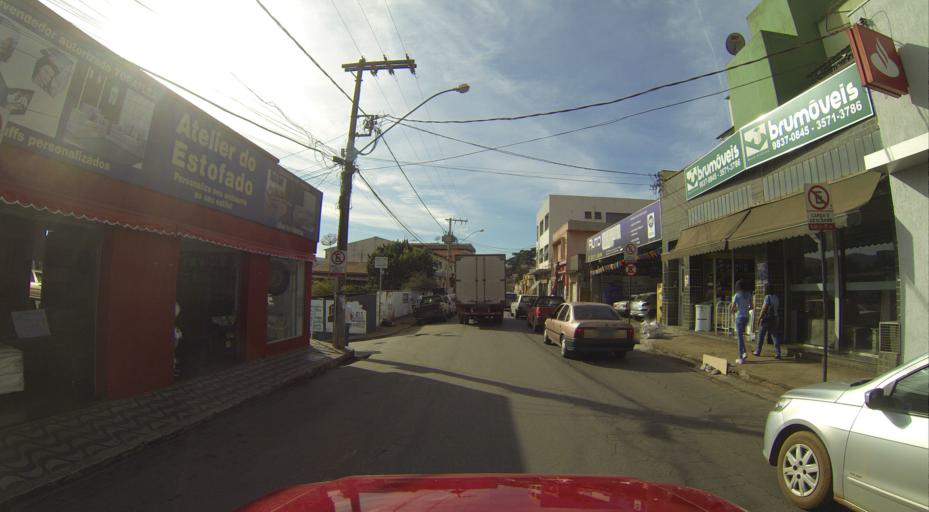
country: BR
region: Minas Gerais
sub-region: Brumadinho
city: Brumadinho
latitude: -20.1438
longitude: -44.2011
